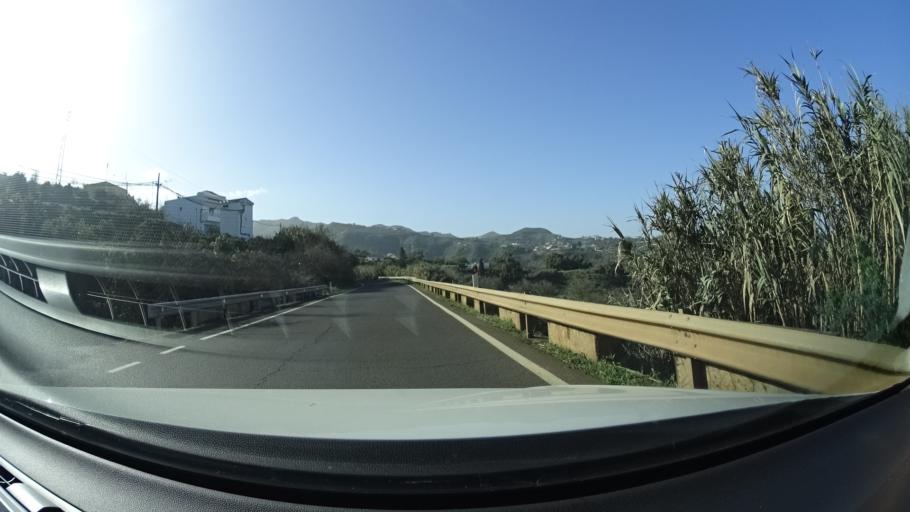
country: ES
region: Canary Islands
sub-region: Provincia de Las Palmas
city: Vega de San Mateo
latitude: 28.0156
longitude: -15.5376
